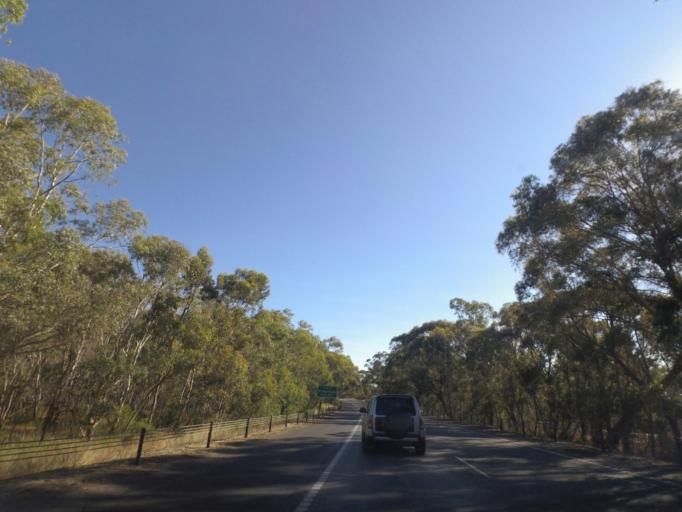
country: AU
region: Victoria
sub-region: Murrindindi
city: Kinglake West
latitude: -37.1770
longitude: 145.0714
